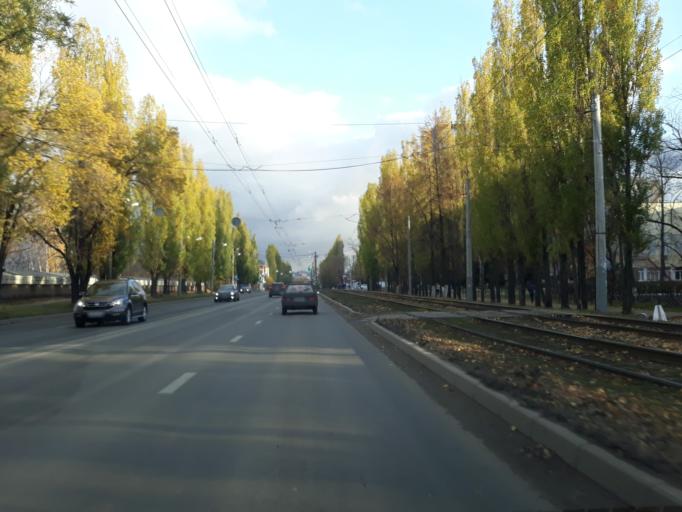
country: RU
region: Nizjnij Novgorod
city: Nizhniy Novgorod
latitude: 56.3345
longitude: 43.8908
